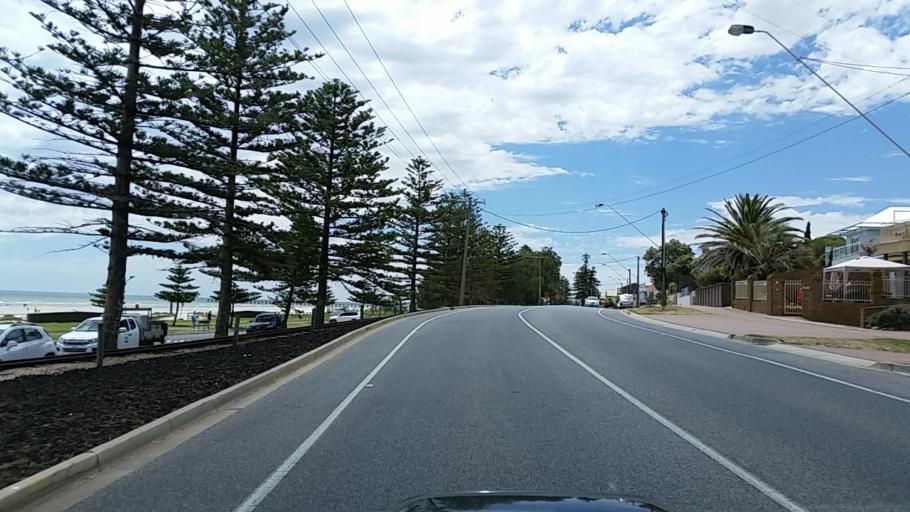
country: AU
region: South Australia
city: Port Adelaide
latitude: -34.8478
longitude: 138.4774
